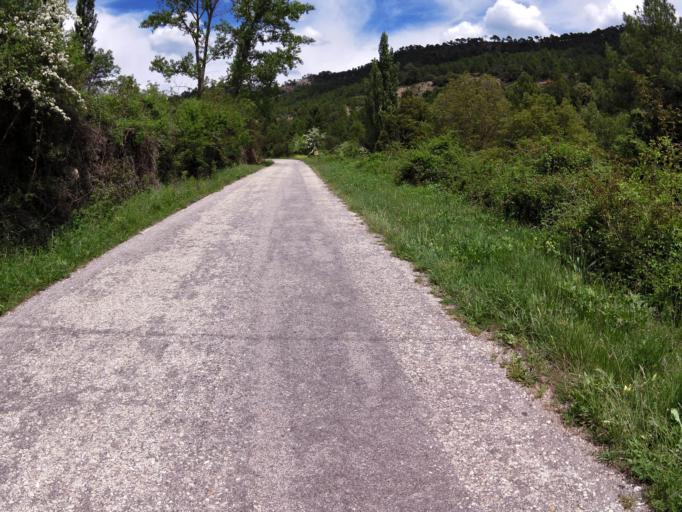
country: ES
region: Castille-La Mancha
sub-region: Provincia de Albacete
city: Paterna del Madera
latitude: 38.5767
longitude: -2.3382
